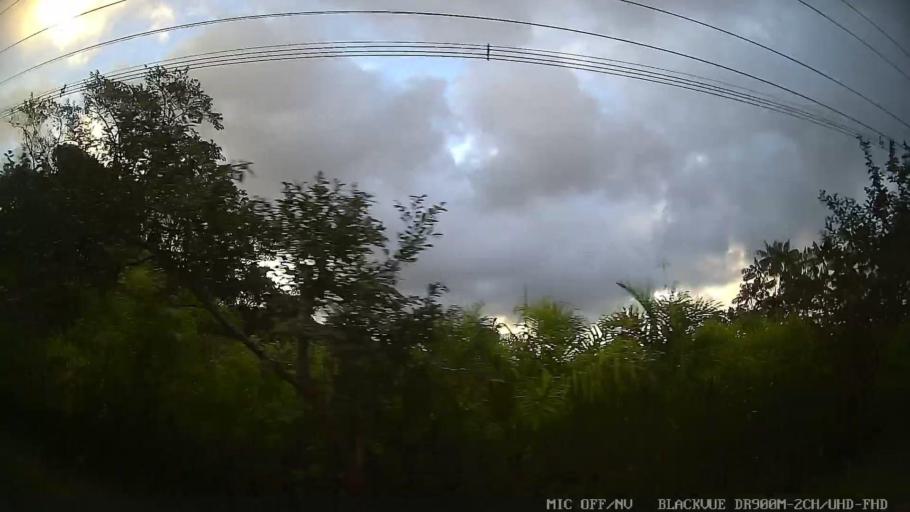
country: BR
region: Sao Paulo
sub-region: Itanhaem
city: Itanhaem
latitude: -24.1021
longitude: -46.8041
